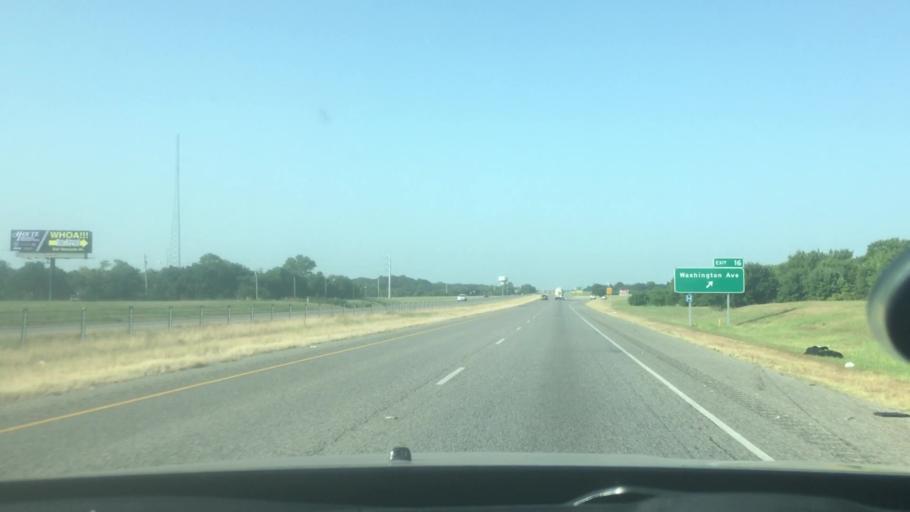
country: US
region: Oklahoma
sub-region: Bryan County
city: Durant
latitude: 34.0262
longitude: -96.3860
